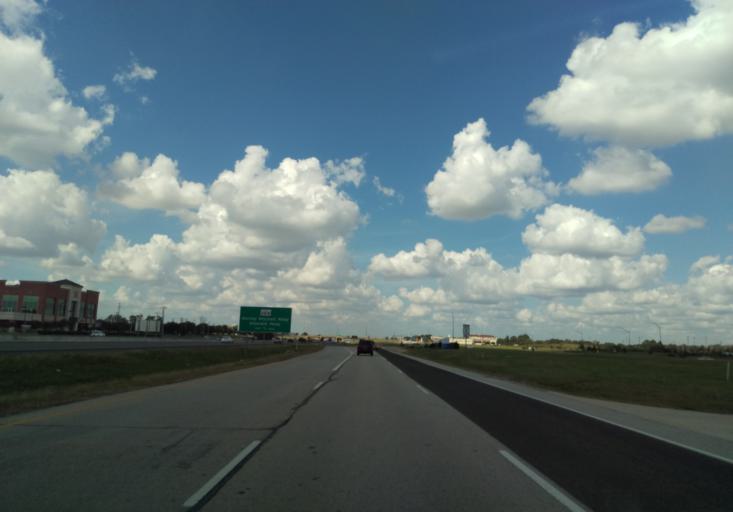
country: US
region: Texas
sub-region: Brazos County
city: College Station
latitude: 30.5786
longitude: -96.2807
